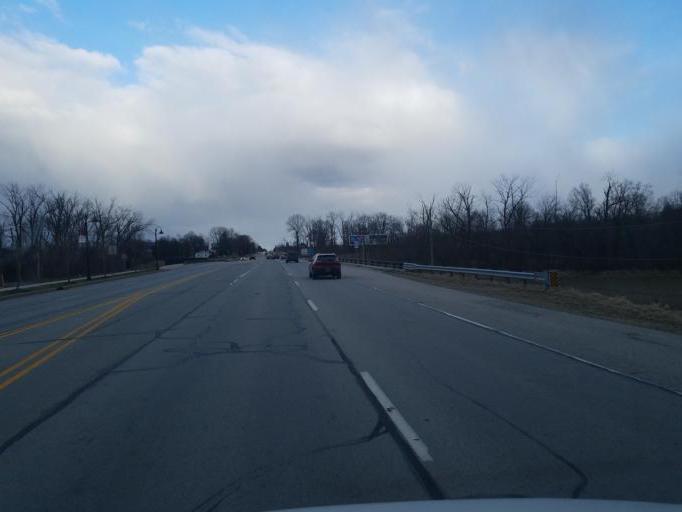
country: US
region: Indiana
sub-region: Marion County
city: Cumberland
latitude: 39.7768
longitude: -85.9499
